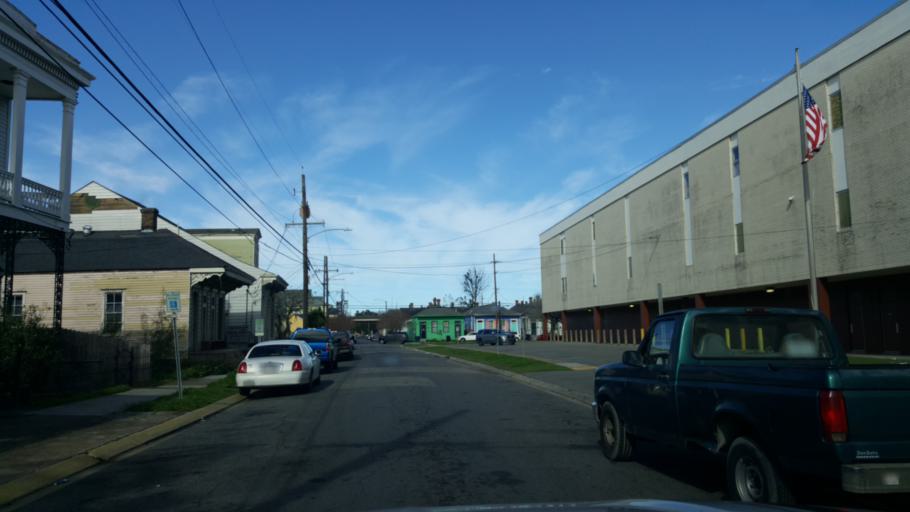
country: US
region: Louisiana
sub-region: Orleans Parish
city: New Orleans
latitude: 29.9684
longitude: -90.0653
